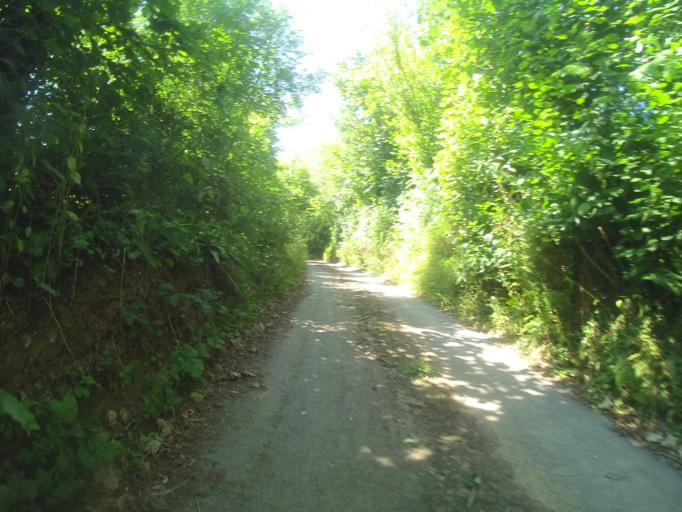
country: GB
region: England
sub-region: Devon
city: Dartmouth
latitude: 50.3589
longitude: -3.6167
